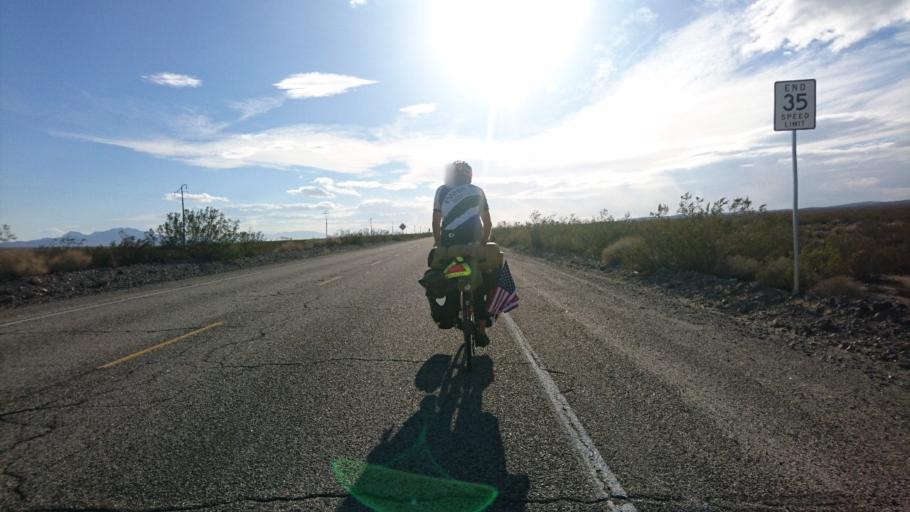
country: US
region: California
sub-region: San Bernardino County
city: Needles
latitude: 34.6872
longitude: -115.3166
